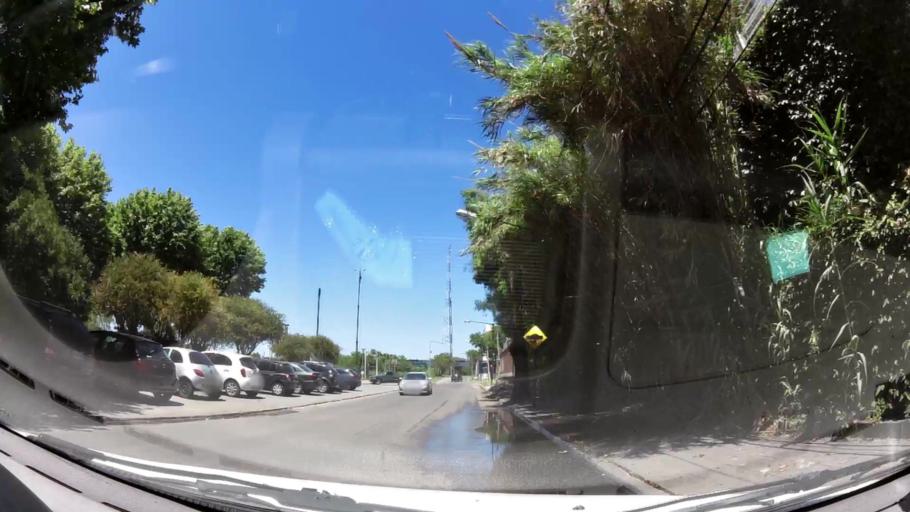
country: AR
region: Buenos Aires
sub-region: Partido de Vicente Lopez
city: Olivos
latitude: -34.4897
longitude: -58.4813
